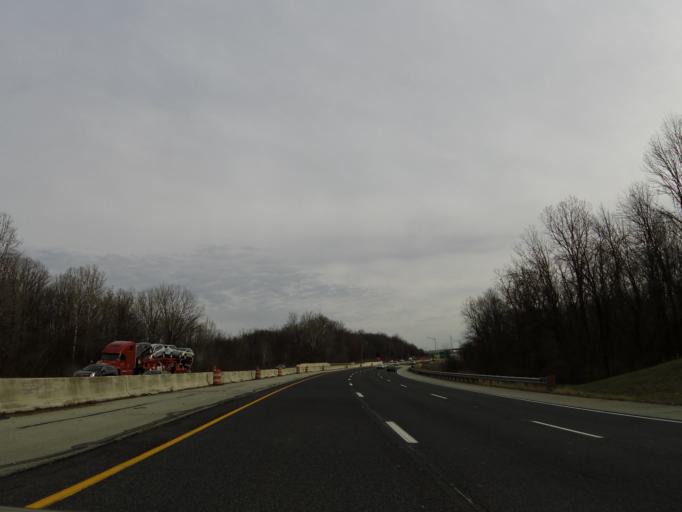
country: US
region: Indiana
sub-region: Marion County
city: Meridian Hills
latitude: 39.9297
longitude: -86.1747
